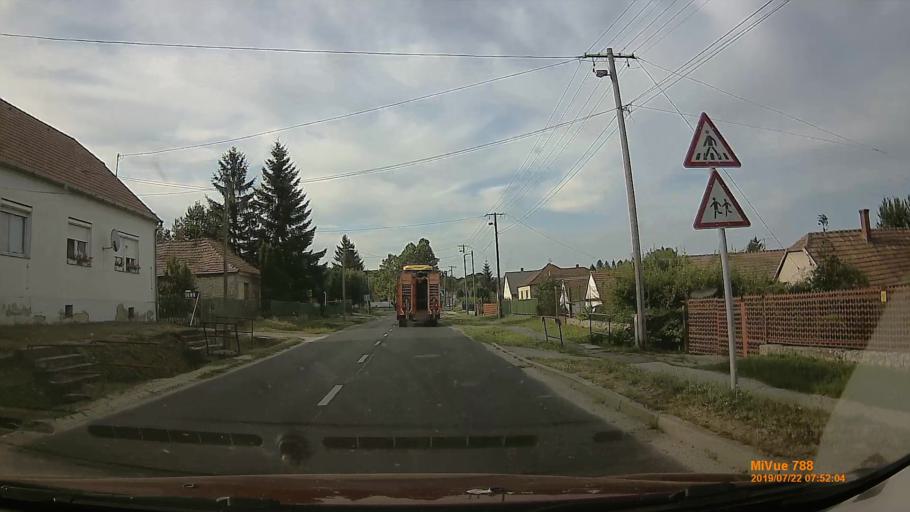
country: HU
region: Veszprem
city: Ajka
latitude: 47.0548
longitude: 17.5553
